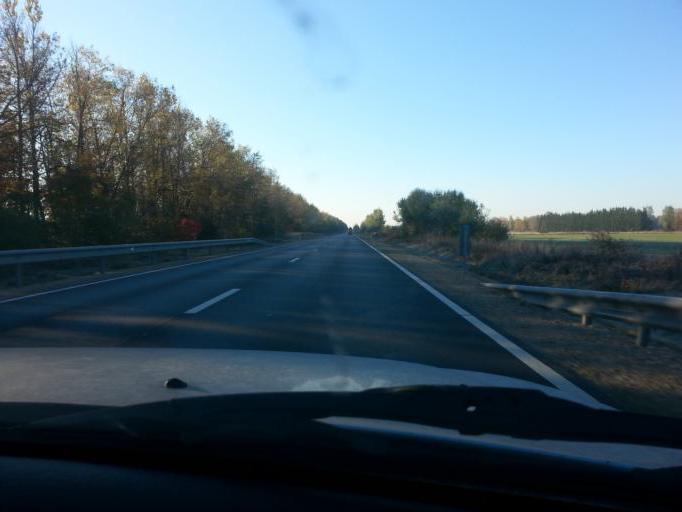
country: LV
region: Jelgava
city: Jelgava
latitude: 56.5171
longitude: 23.7030
